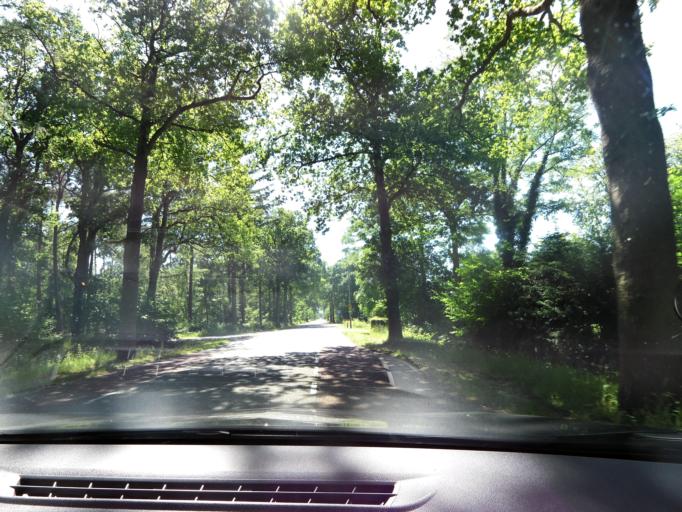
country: NL
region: Overijssel
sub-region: Gemeente Hof van Twente
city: Diepenheim
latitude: 52.2109
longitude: 6.5718
